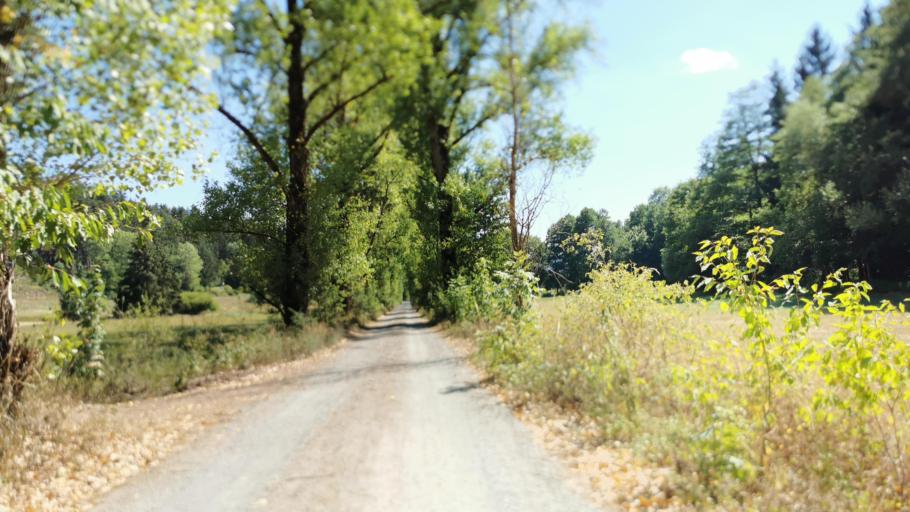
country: DE
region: Bavaria
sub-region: Upper Franconia
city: Pressig
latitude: 50.3753
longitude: 11.3057
